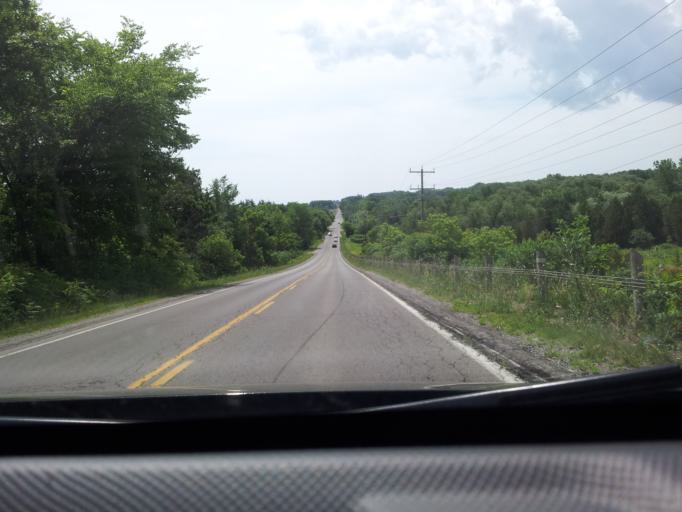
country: CA
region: Ontario
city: Norfolk County
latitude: 42.8127
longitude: -80.2489
